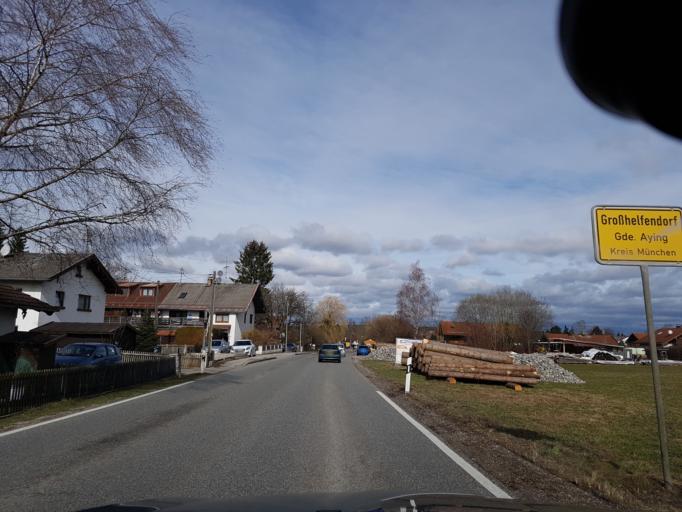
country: DE
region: Bavaria
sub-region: Upper Bavaria
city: Aying
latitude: 47.9400
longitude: 11.7954
